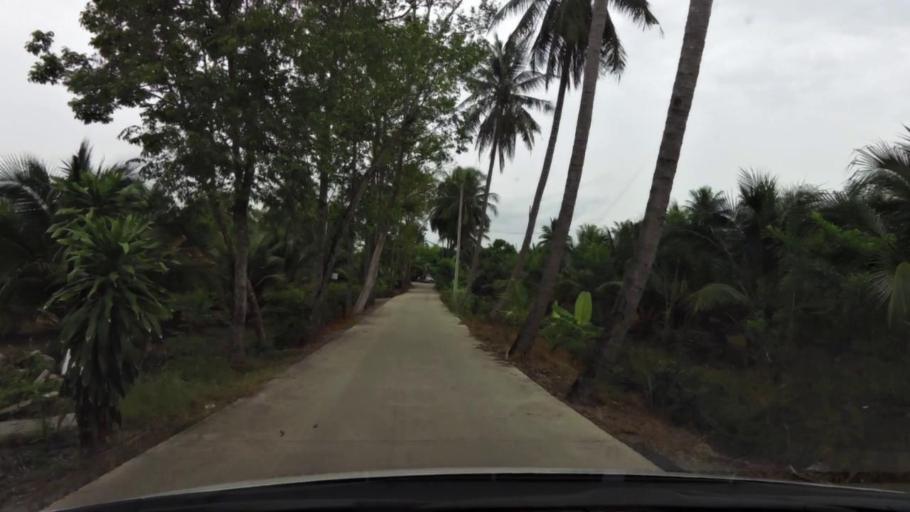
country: TH
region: Samut Sakhon
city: Ban Phaeo
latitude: 13.5967
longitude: 100.0293
